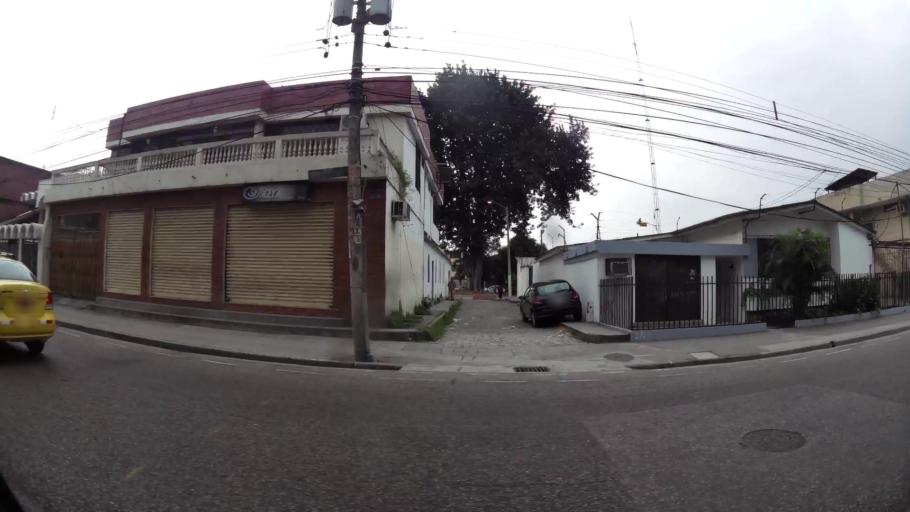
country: EC
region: Guayas
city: Eloy Alfaro
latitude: -2.1708
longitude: -79.8847
